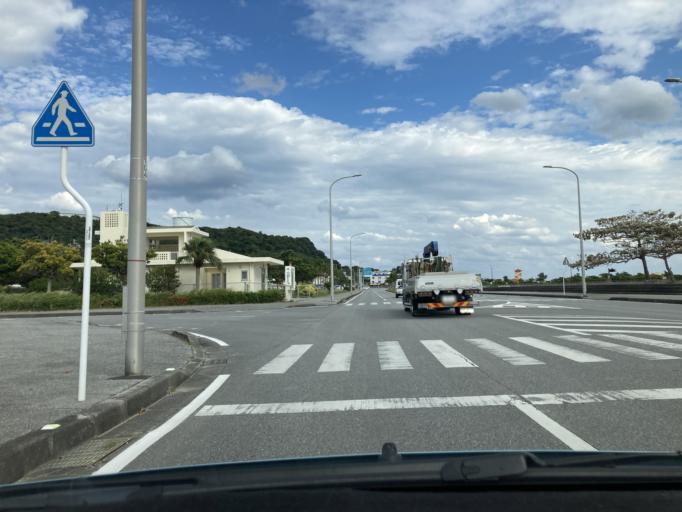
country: JP
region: Okinawa
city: Katsuren-haebaru
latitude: 26.3403
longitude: 127.9518
